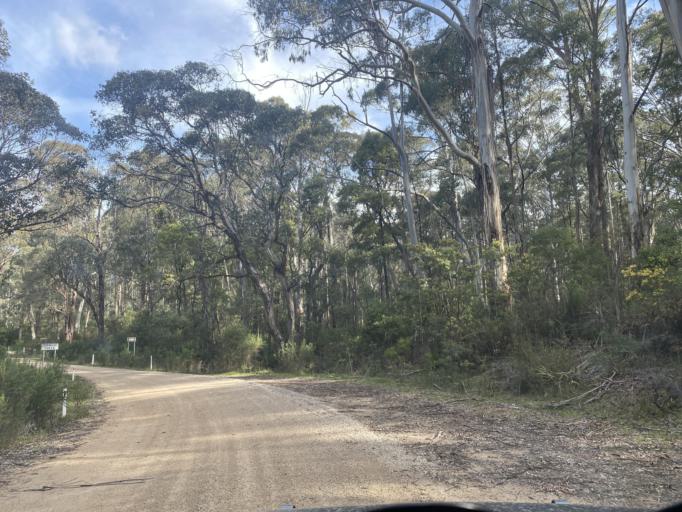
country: AU
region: Victoria
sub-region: Mansfield
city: Mansfield
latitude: -36.8645
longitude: 146.1979
